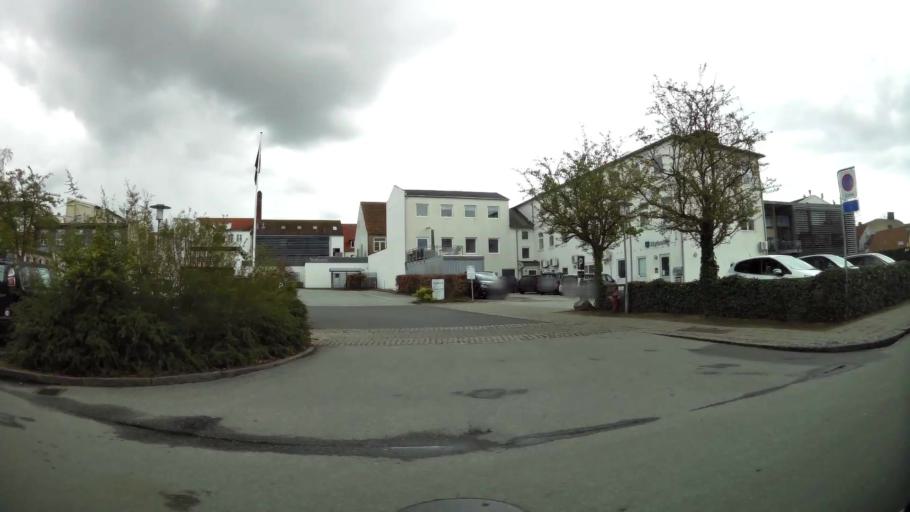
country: DK
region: South Denmark
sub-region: Haderslev Kommune
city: Haderslev
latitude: 55.2506
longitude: 9.4839
